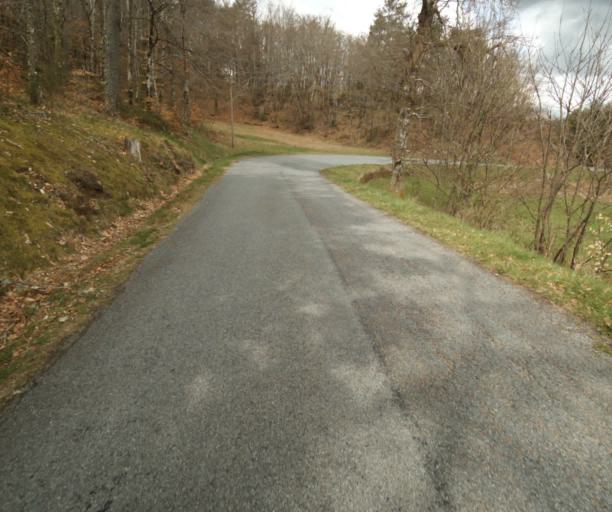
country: FR
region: Limousin
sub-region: Departement de la Correze
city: Correze
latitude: 45.3273
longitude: 1.9540
